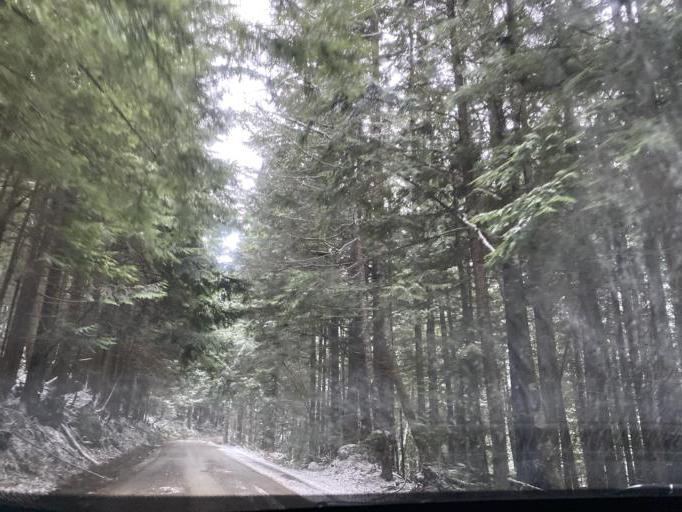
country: US
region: Washington
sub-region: King County
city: Tanner
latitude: 47.3927
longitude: -121.4790
